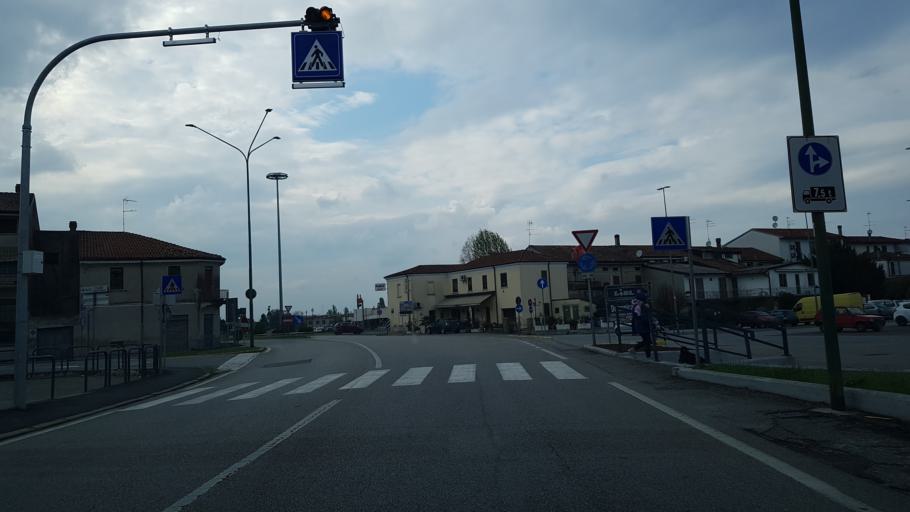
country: IT
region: Lombardy
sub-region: Provincia di Mantova
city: Ostiglia
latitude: 45.0711
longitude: 11.1352
